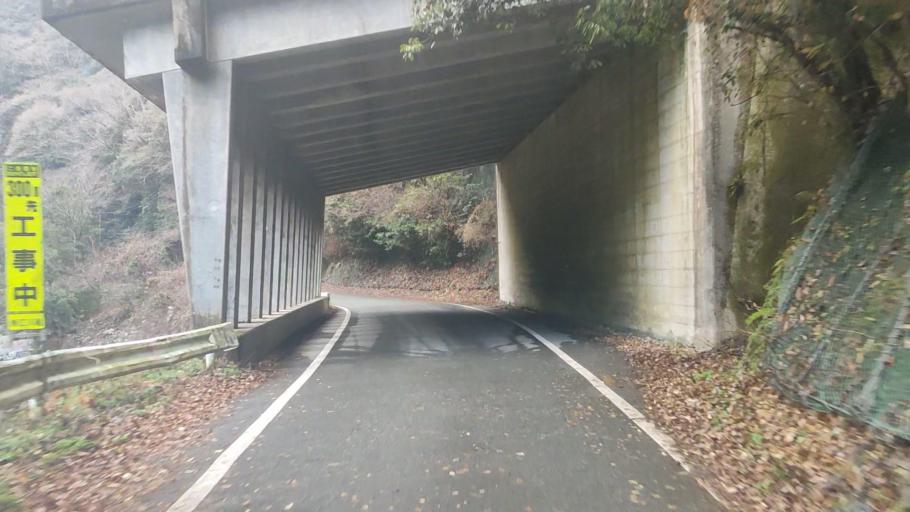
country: JP
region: Kumamoto
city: Matsubase
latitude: 32.4836
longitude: 130.8900
